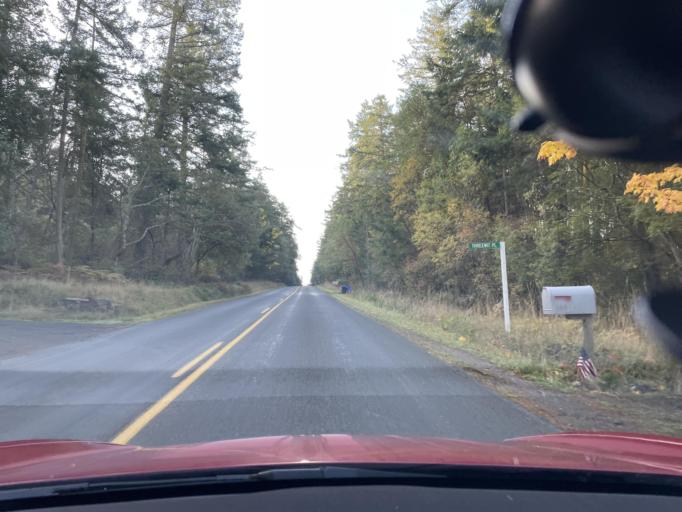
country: US
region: Washington
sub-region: San Juan County
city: Friday Harbor
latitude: 48.5476
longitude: -123.1589
